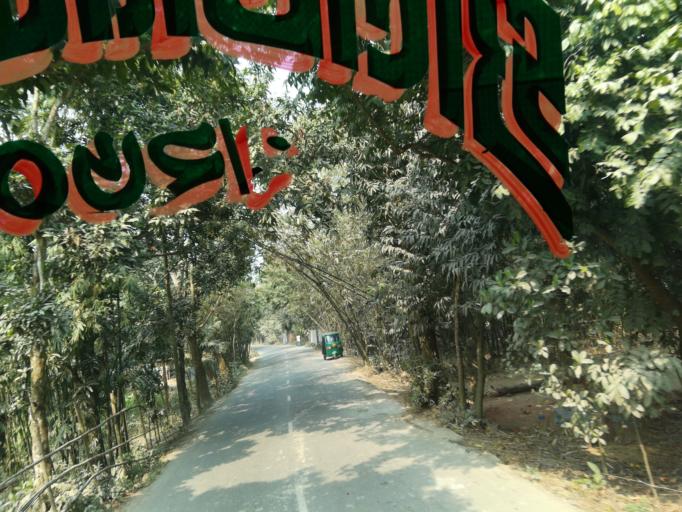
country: BD
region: Dhaka
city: Nagarpur
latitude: 23.9844
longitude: 89.8440
